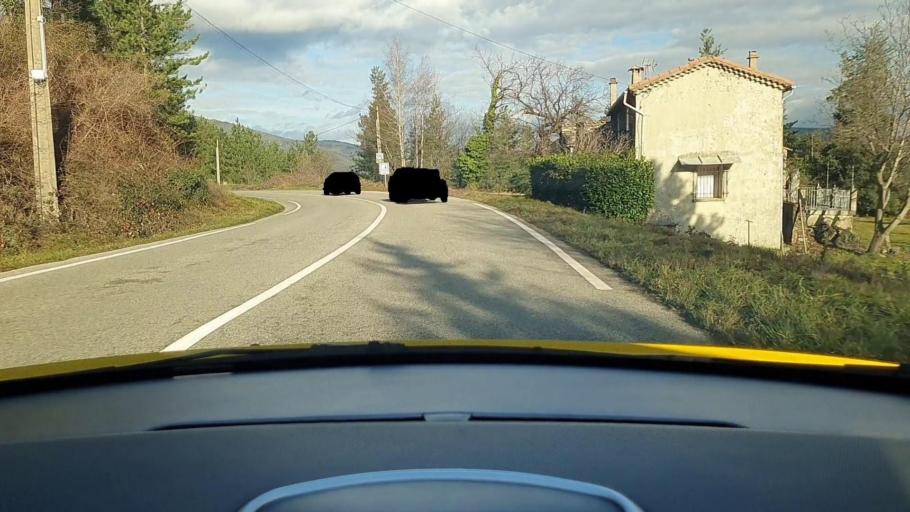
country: FR
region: Languedoc-Roussillon
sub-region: Departement du Gard
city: Branoux-les-Taillades
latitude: 44.3691
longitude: 3.9473
